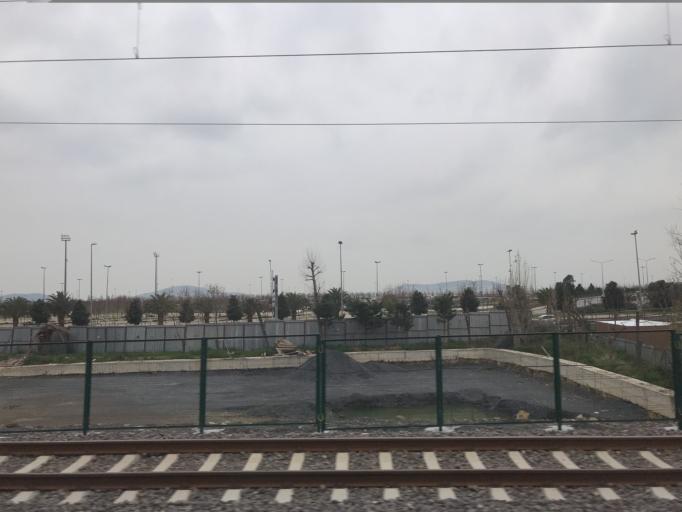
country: TR
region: Istanbul
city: Maltepe
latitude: 40.9323
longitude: 29.1188
